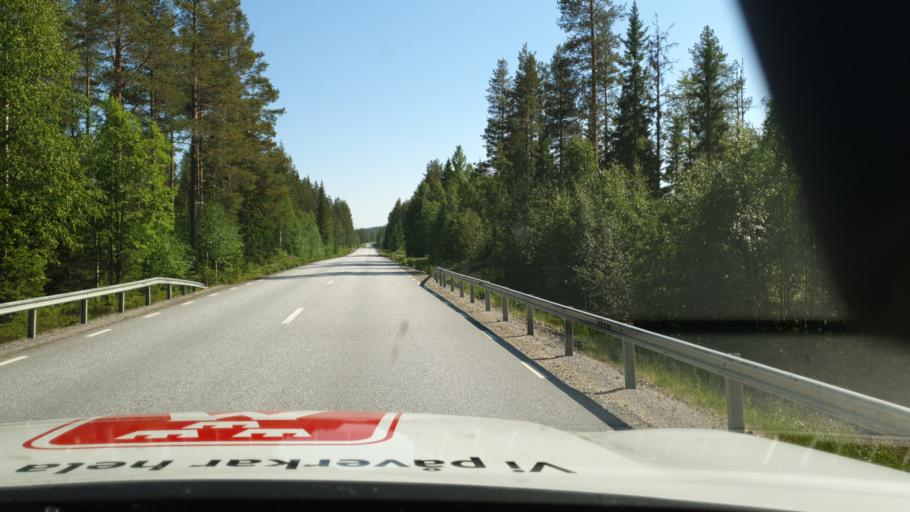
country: SE
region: Vaesterbotten
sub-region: Umea Kommun
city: Ersmark
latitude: 64.2805
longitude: 20.2248
